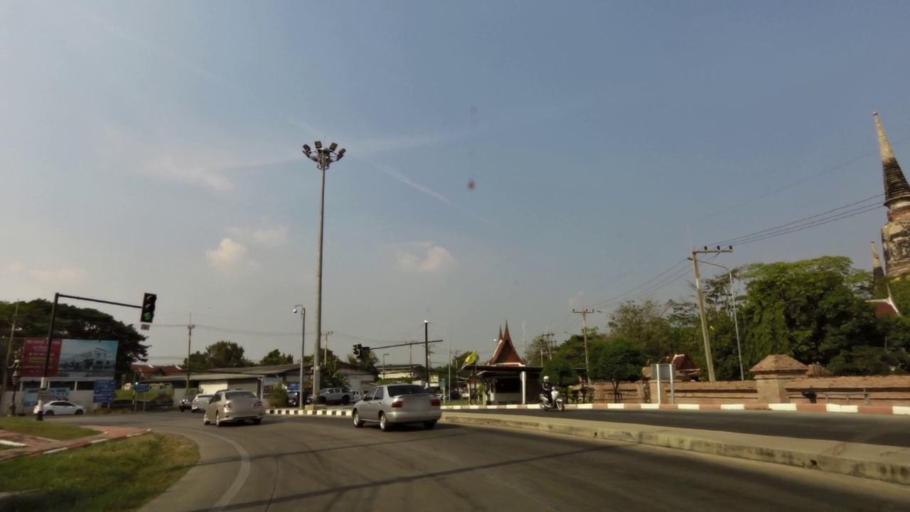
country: TH
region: Phra Nakhon Si Ayutthaya
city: Phra Nakhon Si Ayutthaya
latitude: 14.3442
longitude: 100.5915
